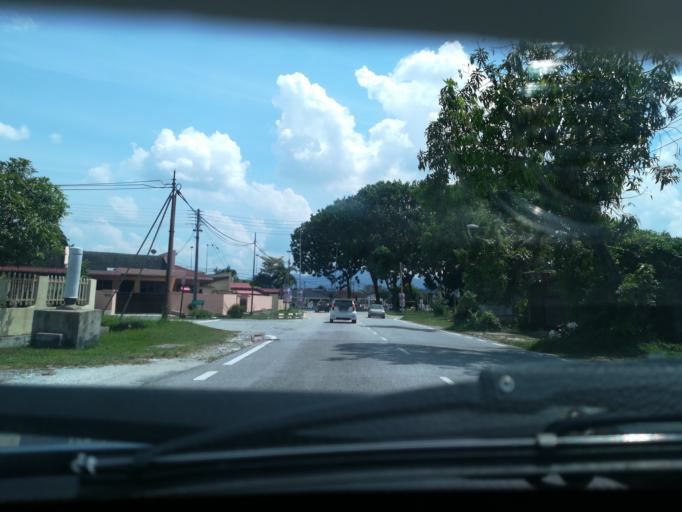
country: MY
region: Perak
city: Ipoh
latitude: 4.6121
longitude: 101.1158
